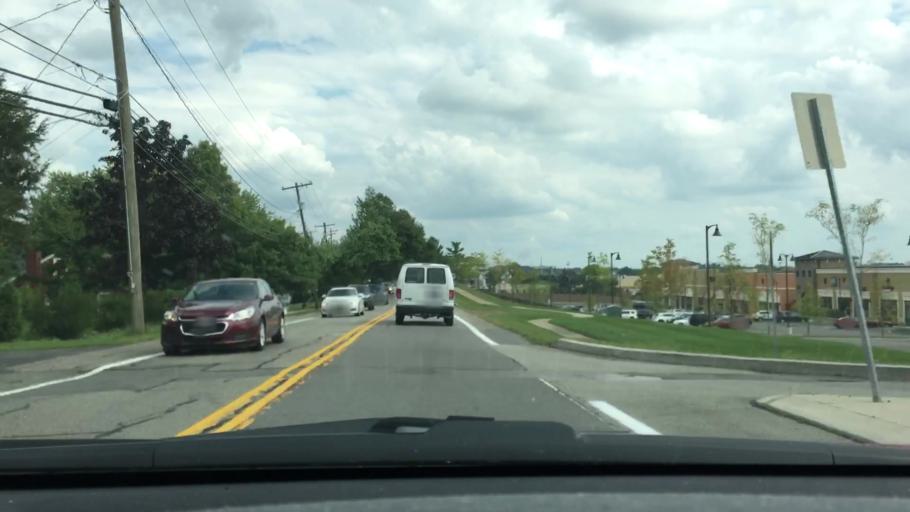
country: US
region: Pennsylvania
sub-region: Allegheny County
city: Mount Lebanon
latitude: 40.3487
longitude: -80.0578
